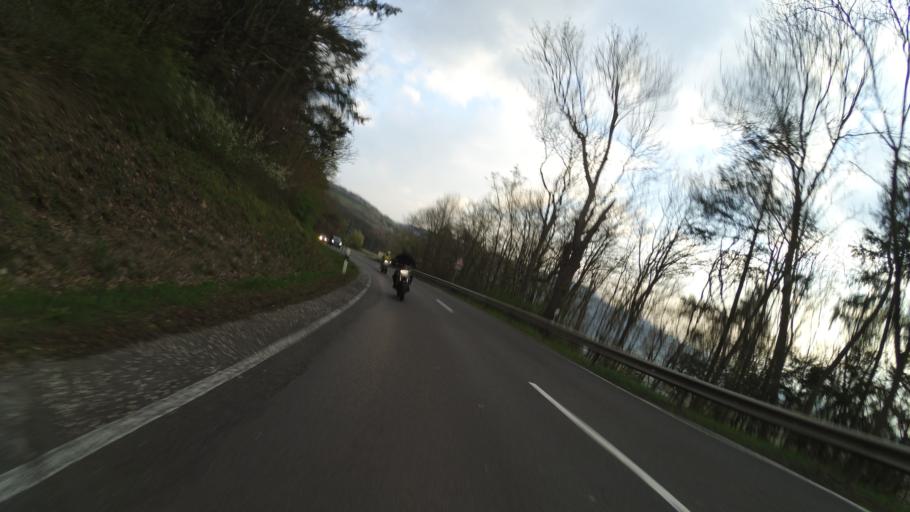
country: DE
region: Rheinland-Pfalz
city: Veldenz
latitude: 49.8999
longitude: 7.0263
